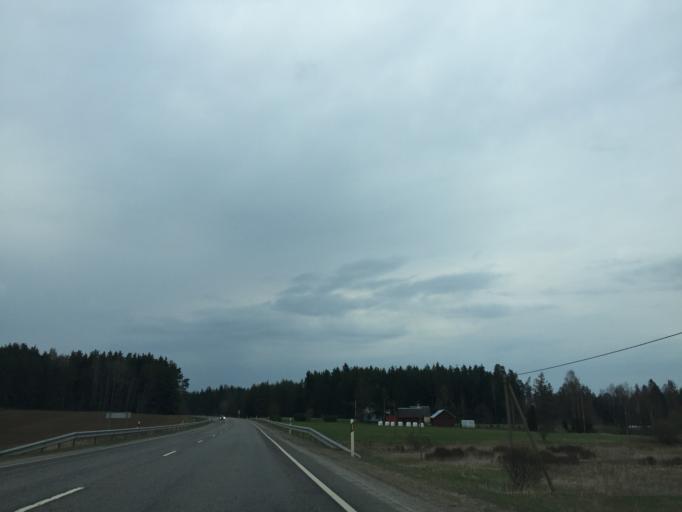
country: EE
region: Tartu
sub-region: UElenurme vald
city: Ulenurme
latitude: 58.0943
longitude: 26.7377
